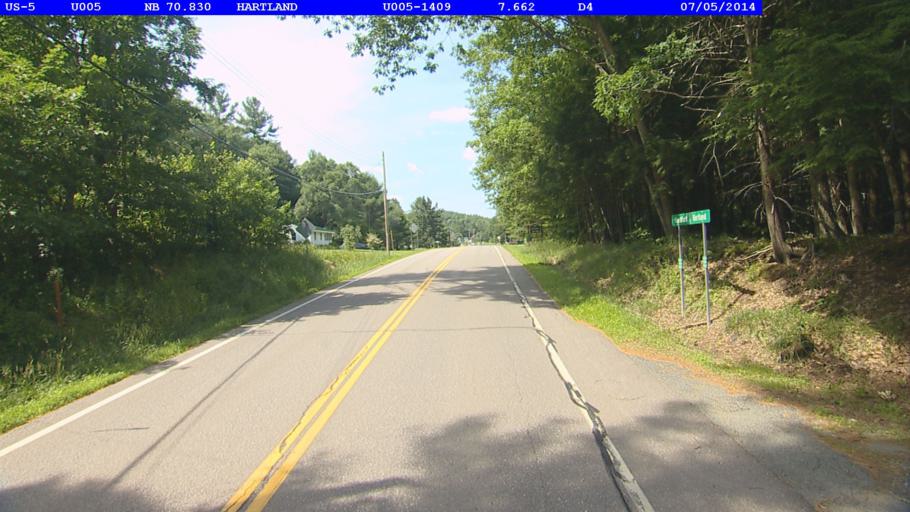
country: US
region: Vermont
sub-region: Windsor County
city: White River Junction
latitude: 43.6107
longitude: -72.3539
